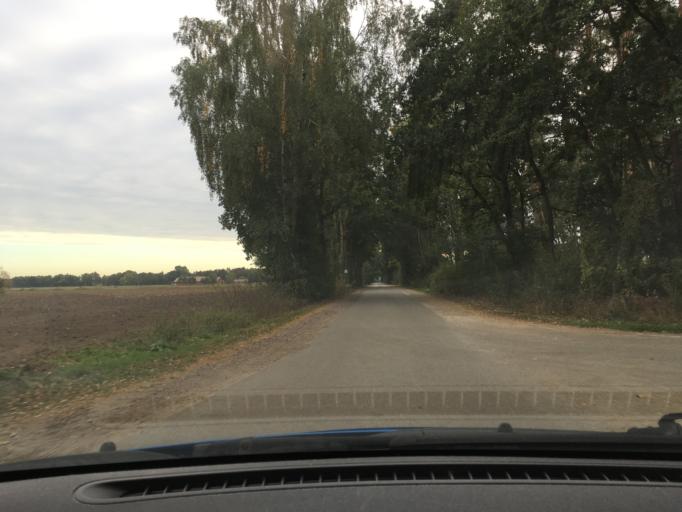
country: DE
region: Lower Saxony
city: Winsen
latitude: 53.3633
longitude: 10.2353
